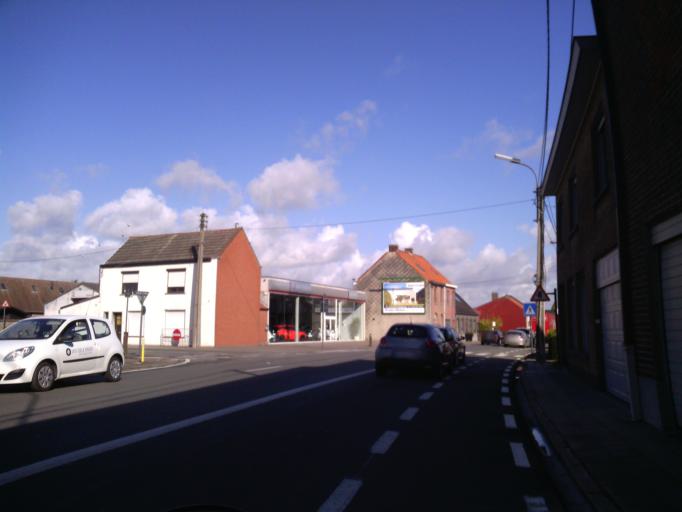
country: BE
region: Flanders
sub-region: Provincie West-Vlaanderen
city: Wevelgem
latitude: 50.7763
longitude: 3.1700
